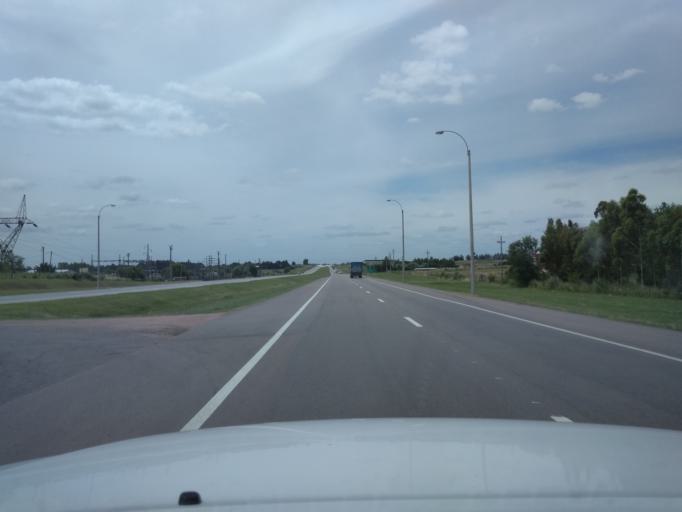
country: UY
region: Canelones
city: Las Piedras
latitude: -34.7156
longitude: -56.2440
